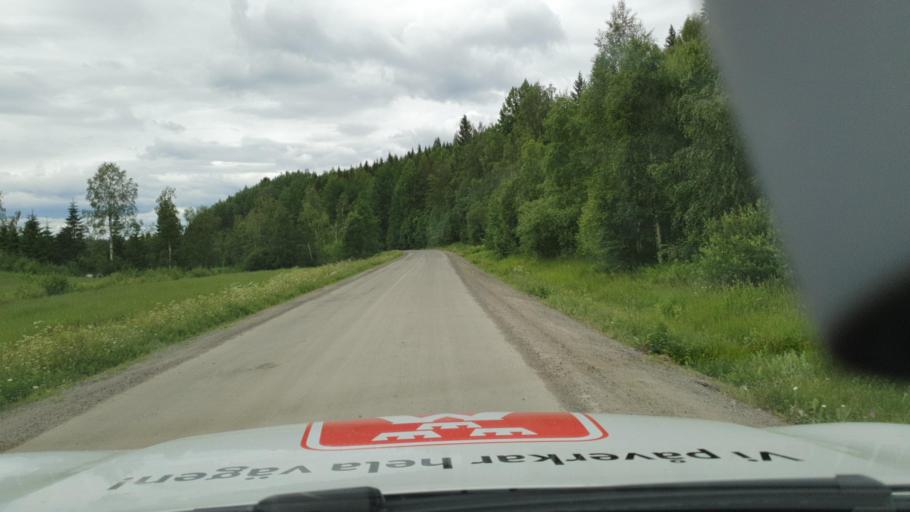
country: SE
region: Vaesterbotten
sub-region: Nordmalings Kommun
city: Nordmaling
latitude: 63.6843
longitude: 19.4511
